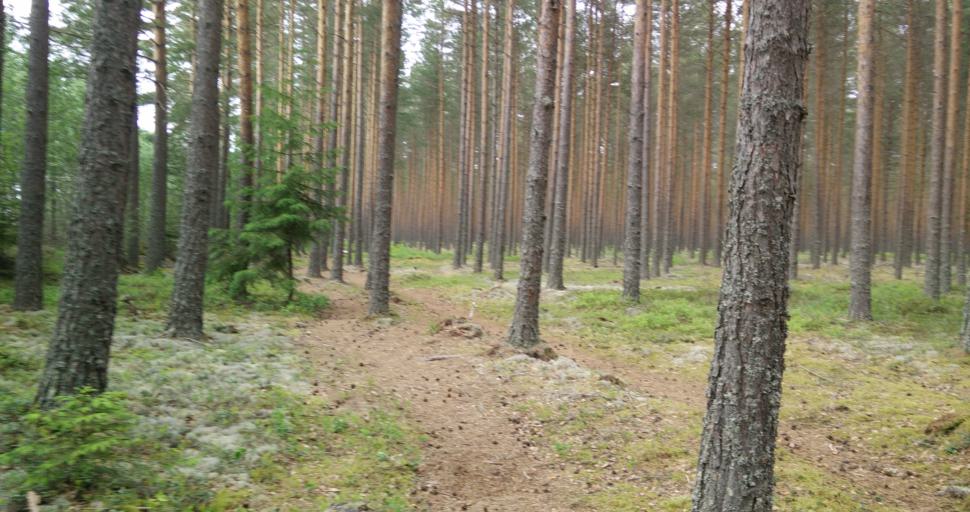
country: SE
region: Vaermland
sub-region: Hagfors Kommun
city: Hagfors
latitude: 60.0138
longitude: 13.5840
